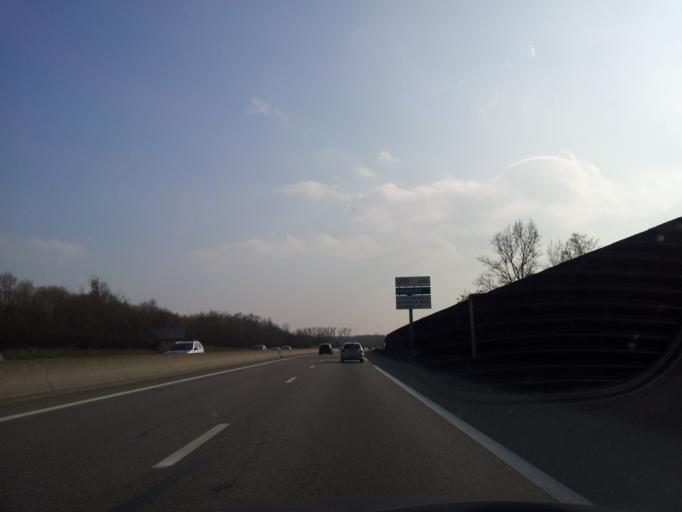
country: FR
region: Alsace
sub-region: Departement du Haut-Rhin
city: Horbourg-Wihr
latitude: 48.0765
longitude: 7.3852
